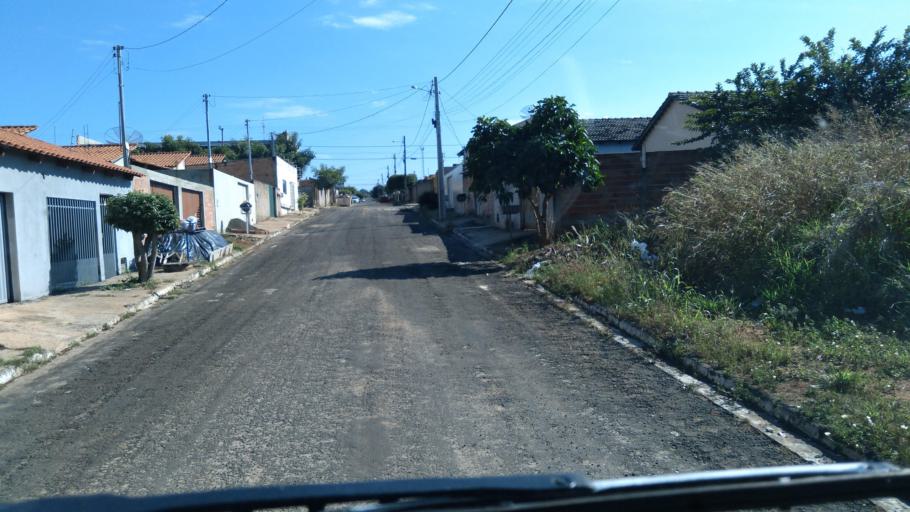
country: BR
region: Goias
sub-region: Mineiros
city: Mineiros
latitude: -17.5761
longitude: -52.5730
